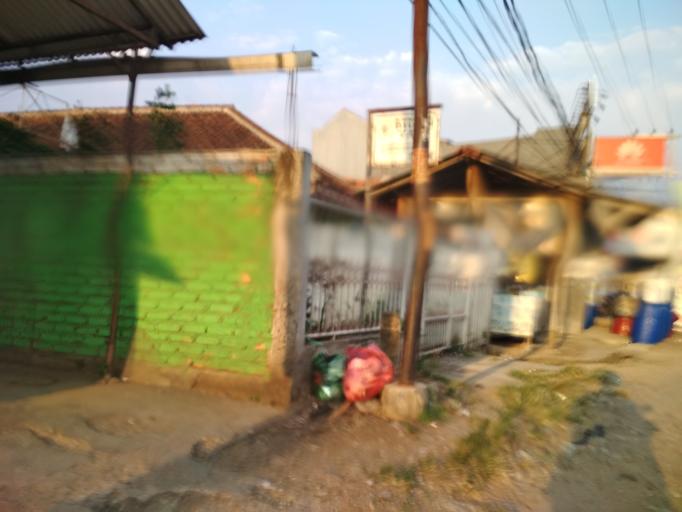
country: ID
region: West Java
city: Ciampea
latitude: -6.5622
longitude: 106.7163
